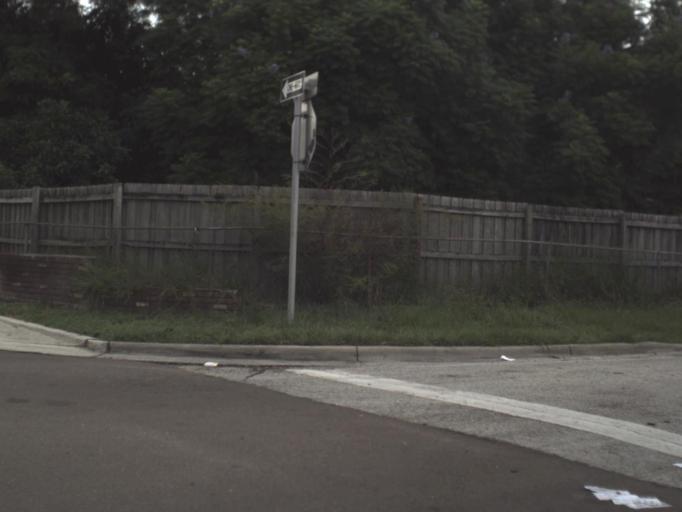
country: US
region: Florida
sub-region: Sarasota County
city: Sarasota Springs
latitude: 27.2989
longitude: -82.4714
